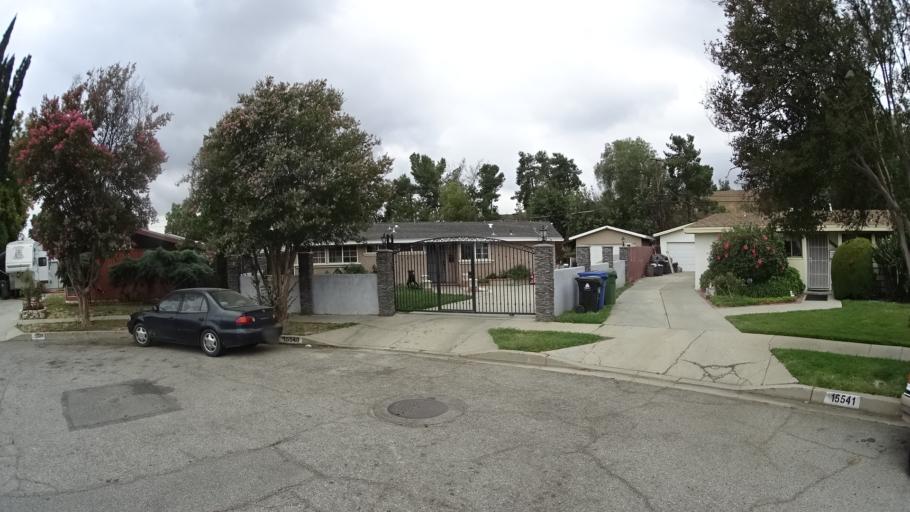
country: US
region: California
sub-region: Los Angeles County
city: San Fernando
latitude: 34.2741
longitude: -118.4706
